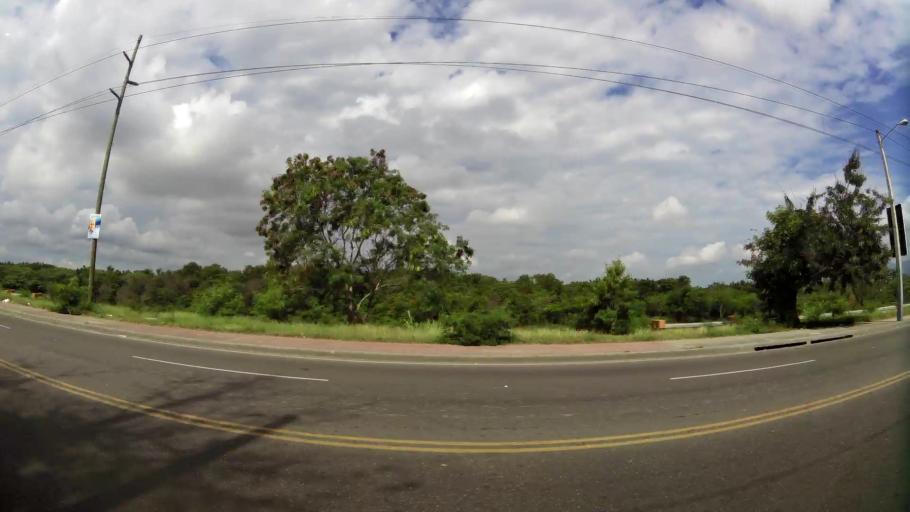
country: DO
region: Santiago
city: Santiago de los Caballeros
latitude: 19.4598
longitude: -70.7143
